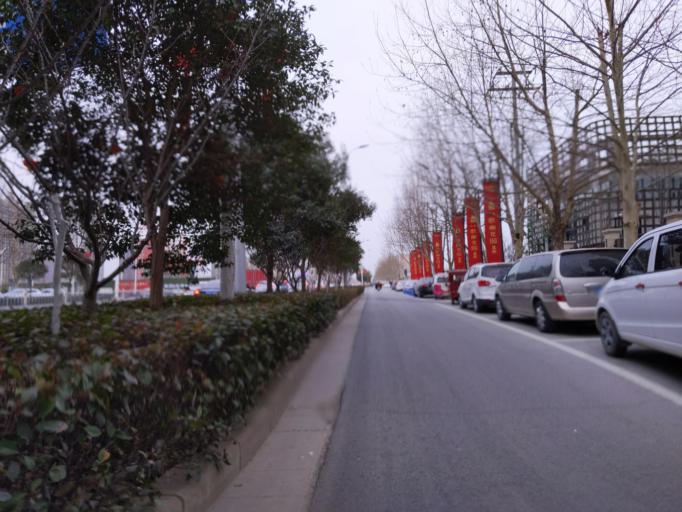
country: CN
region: Henan Sheng
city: Zhongyuanlu
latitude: 35.7573
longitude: 115.0761
